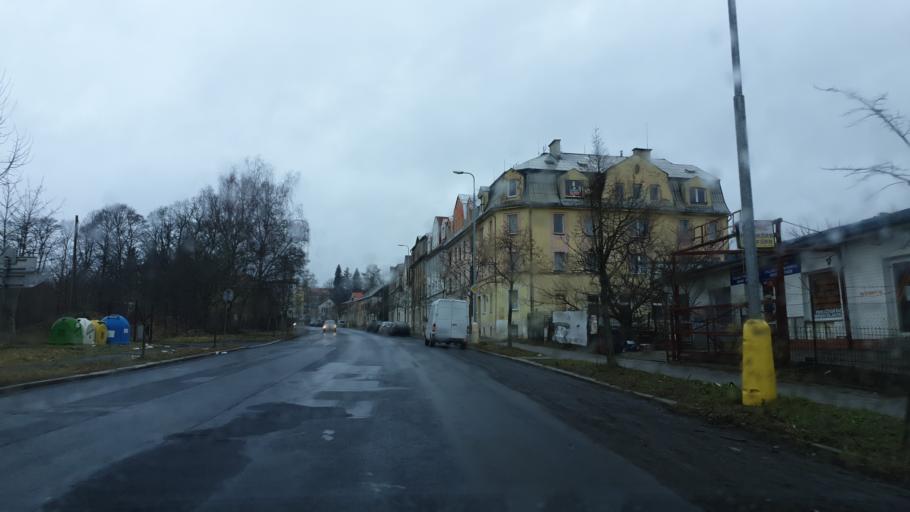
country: CZ
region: Karlovarsky
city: As
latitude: 50.2103
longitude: 12.2037
